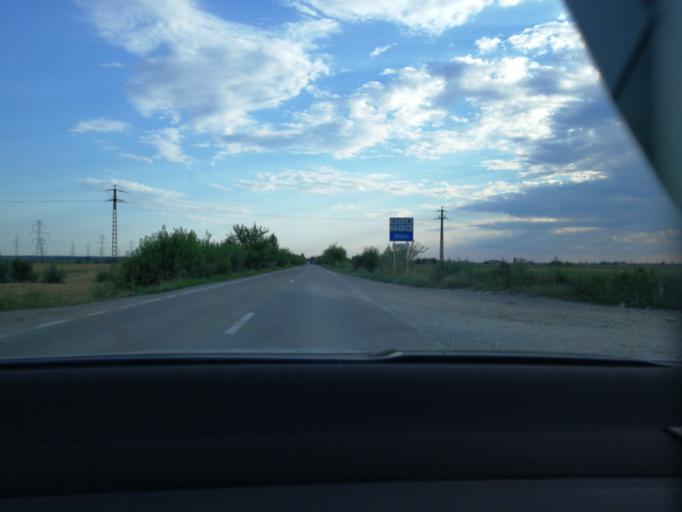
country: RO
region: Prahova
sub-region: Comuna Targsoru Vechi
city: Targsoru Vechi
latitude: 44.8806
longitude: 25.9468
